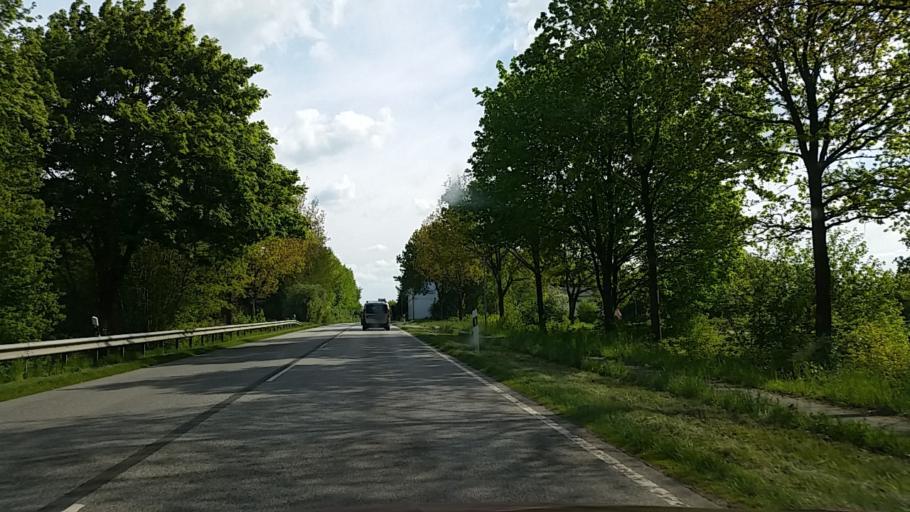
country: DE
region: Schleswig-Holstein
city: Elmenhorst
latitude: 53.7577
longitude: 10.2604
